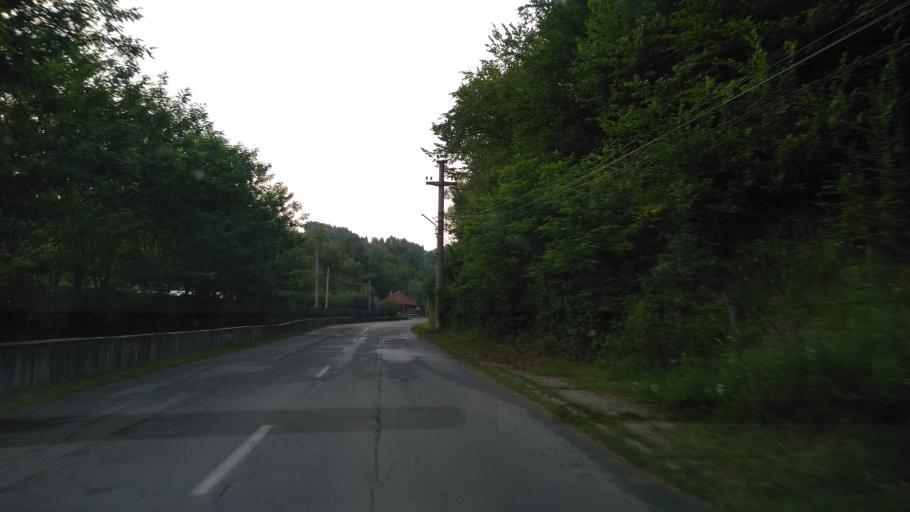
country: RO
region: Hunedoara
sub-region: Comuna Aninoasa
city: Aninoasa
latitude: 45.3928
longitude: 23.3183
